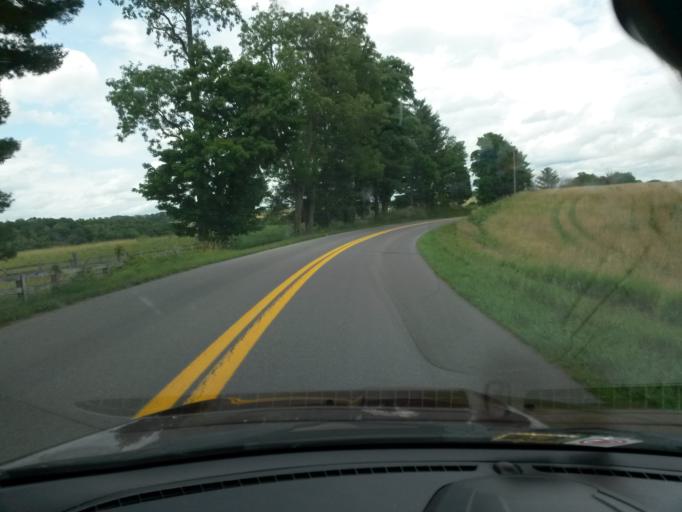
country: US
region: West Virginia
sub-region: Monroe County
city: Union
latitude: 37.5487
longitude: -80.5313
